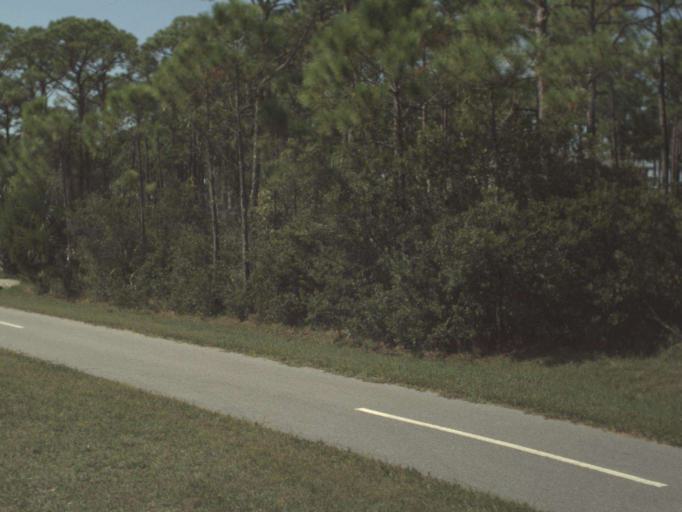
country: US
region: Florida
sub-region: Gulf County
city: Port Saint Joe
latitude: 29.6829
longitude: -85.3299
